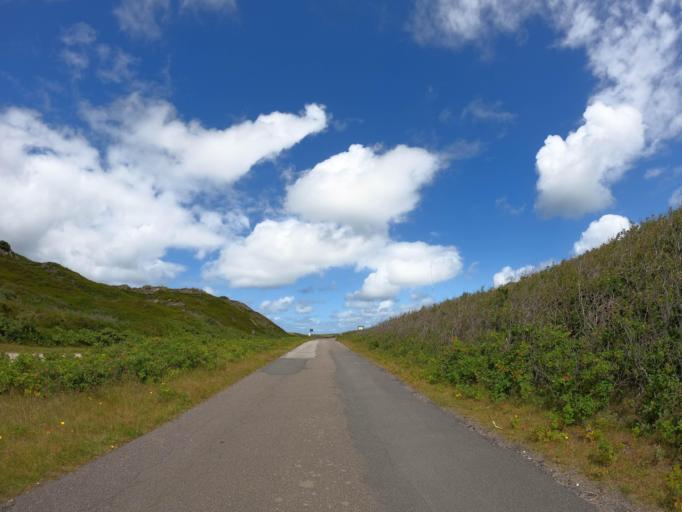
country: DE
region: Schleswig-Holstein
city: Tinnum
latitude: 54.8010
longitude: 8.2918
